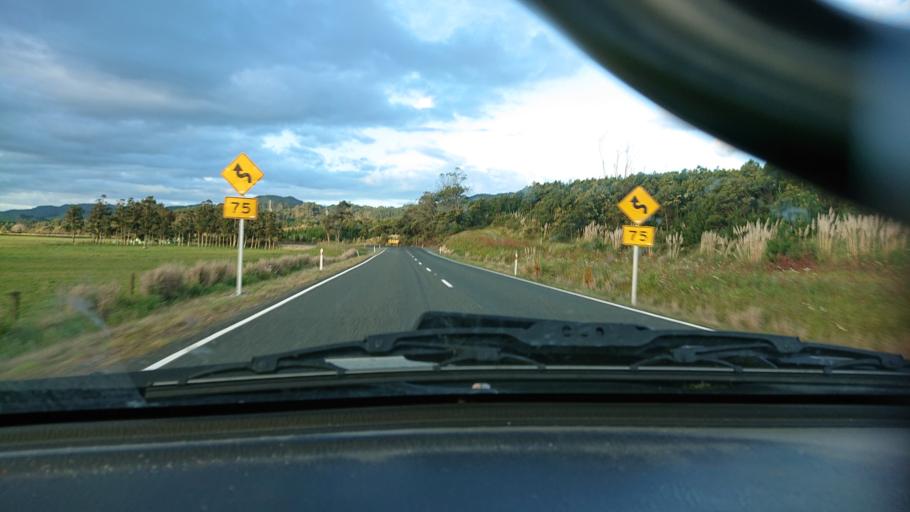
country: NZ
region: Auckland
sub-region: Auckland
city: Parakai
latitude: -36.5151
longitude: 174.4516
